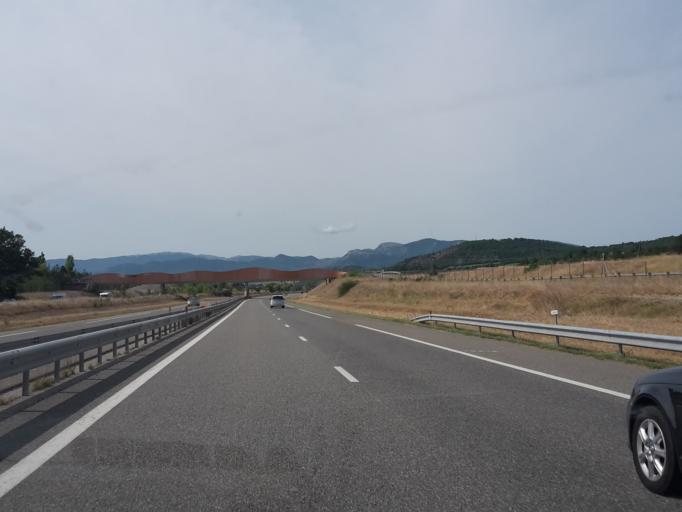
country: FR
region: Provence-Alpes-Cote d'Azur
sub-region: Departement des Hautes-Alpes
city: Laragne-Monteglin
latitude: 44.3569
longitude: 5.9164
